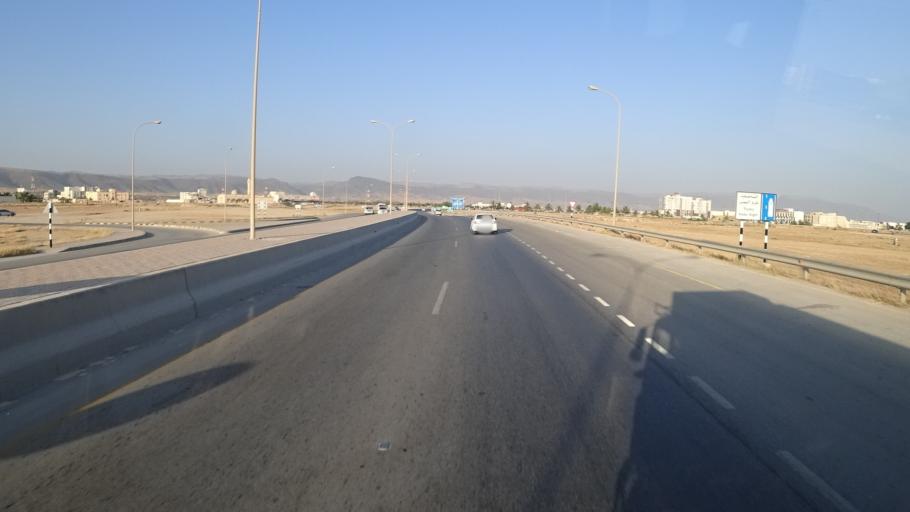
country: OM
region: Zufar
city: Salalah
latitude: 17.0939
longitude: 54.1438
